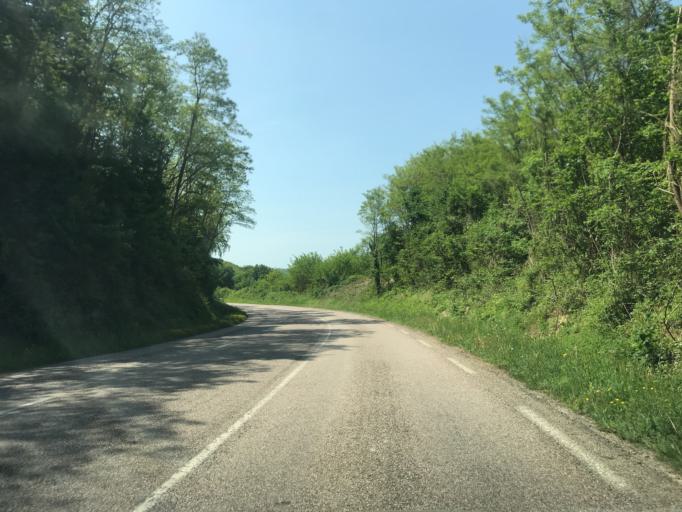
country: FR
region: Haute-Normandie
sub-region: Departement de l'Eure
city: Saint-Aubin-sur-Gaillon
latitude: 49.1123
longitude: 1.2991
